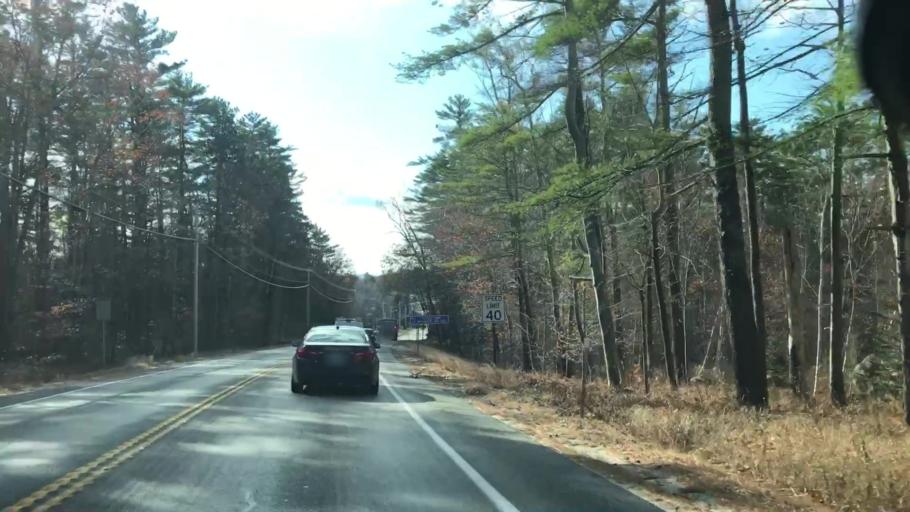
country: US
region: New Hampshire
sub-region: Carroll County
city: Wolfeboro
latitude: 43.6215
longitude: -71.1694
